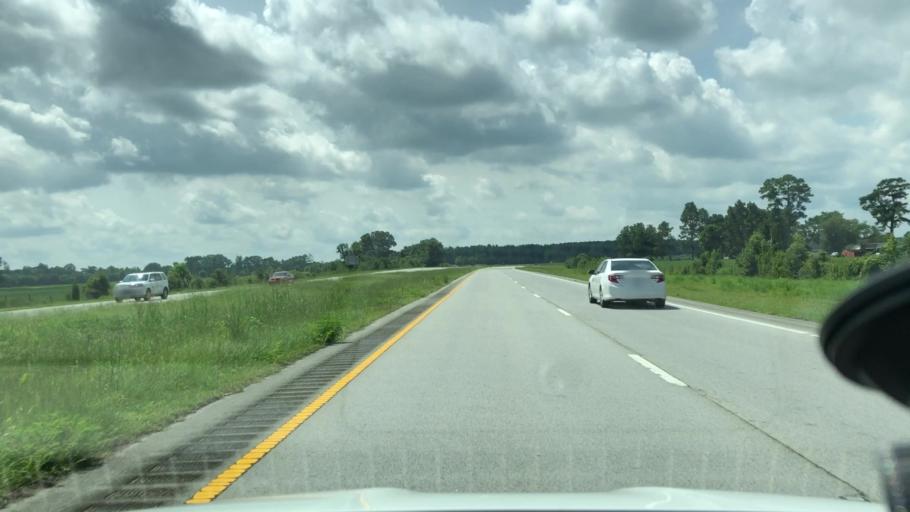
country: US
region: North Carolina
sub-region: Beaufort County
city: Washington
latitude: 35.5137
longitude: -77.0865
